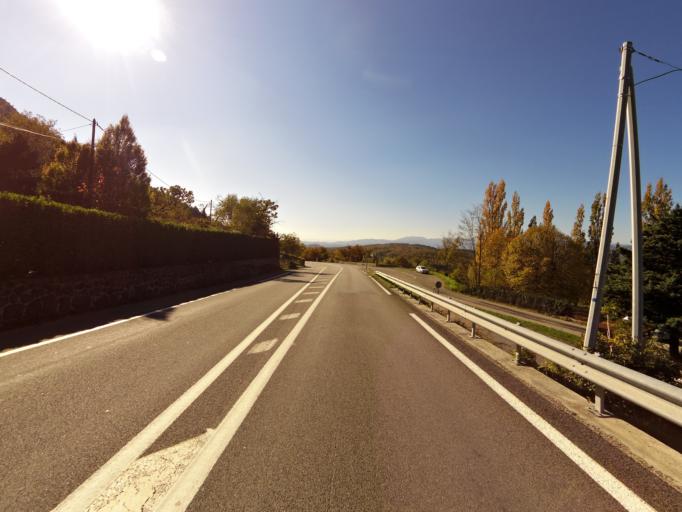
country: FR
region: Rhone-Alpes
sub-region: Departement de l'Ardeche
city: Vesseaux
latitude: 44.6941
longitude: 4.4764
